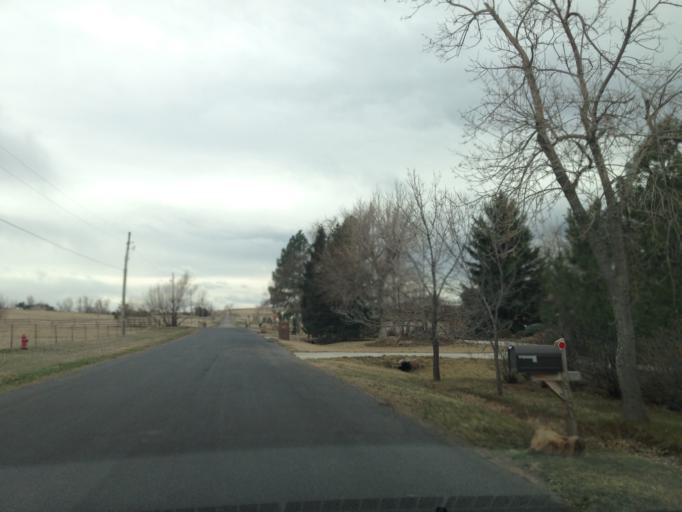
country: US
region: Colorado
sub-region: Boulder County
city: Superior
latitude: 39.9775
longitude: -105.1941
